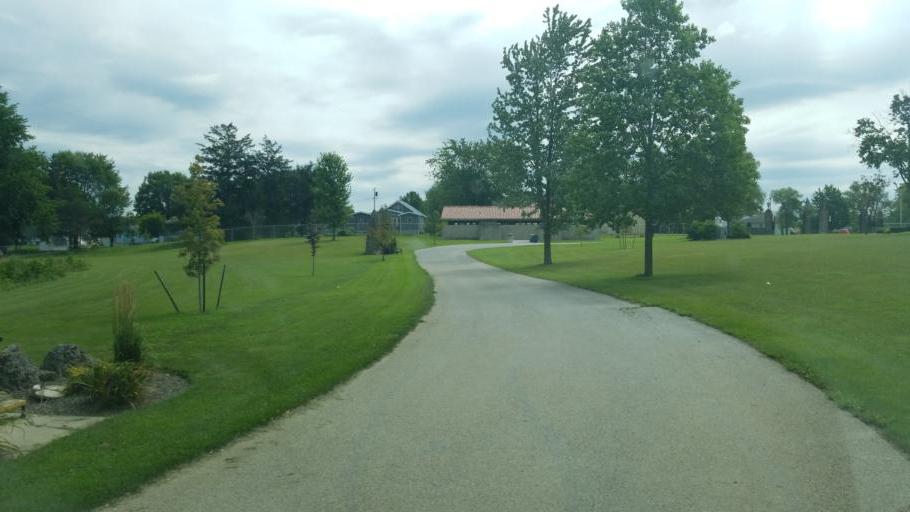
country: US
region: Ohio
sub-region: Wyandot County
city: Carey
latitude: 40.9515
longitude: -83.3934
